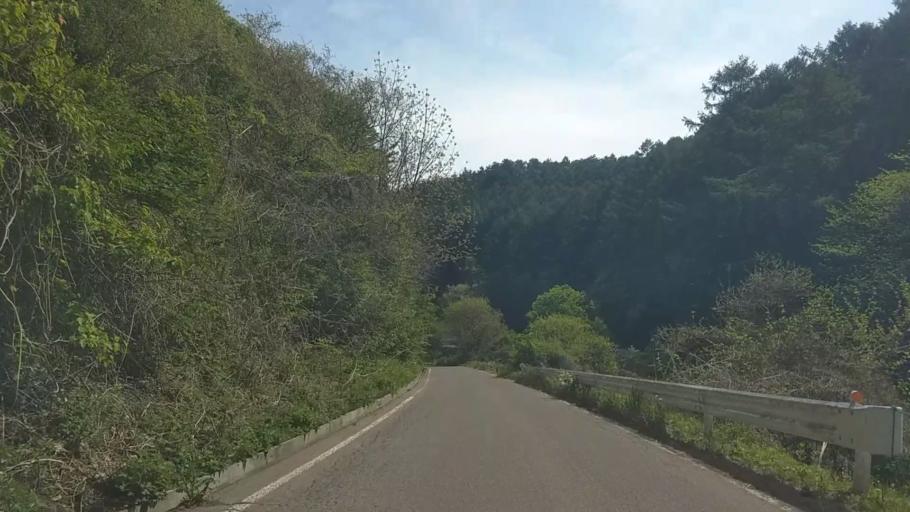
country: JP
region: Nagano
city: Saku
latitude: 36.1089
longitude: 138.4700
